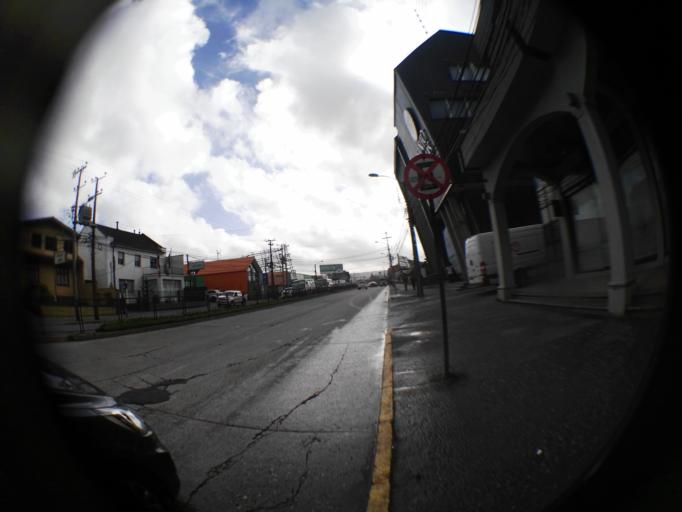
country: CL
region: Los Rios
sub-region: Provincia de Valdivia
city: Valdivia
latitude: -39.8176
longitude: -73.2335
